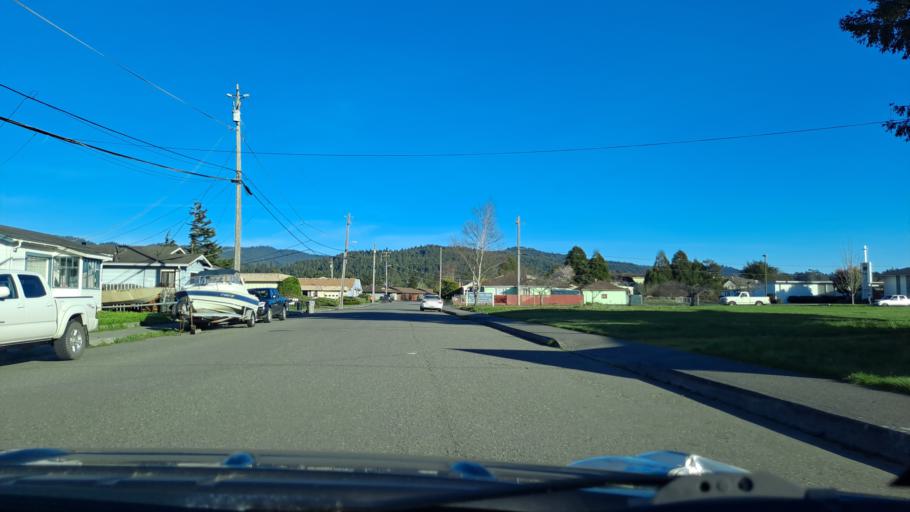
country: US
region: California
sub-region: Humboldt County
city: Fortuna
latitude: 40.5920
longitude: -124.1455
